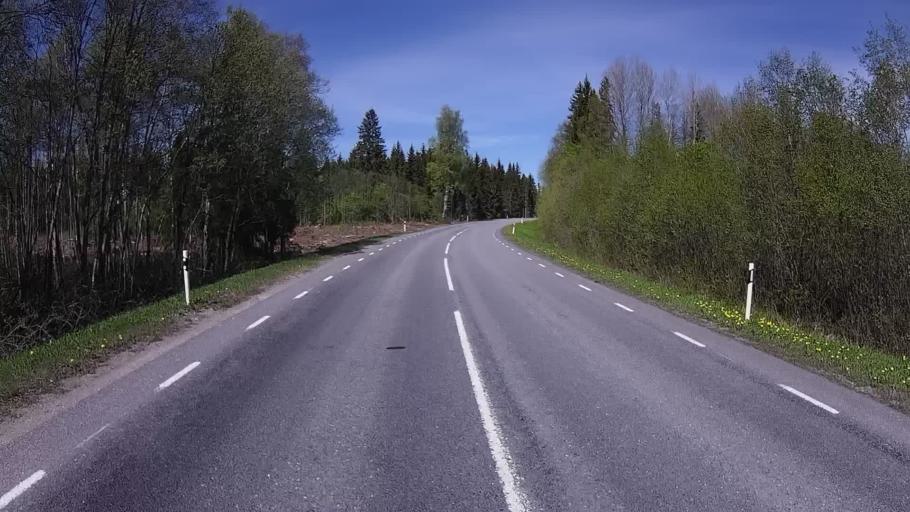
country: EE
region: Raplamaa
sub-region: Kehtna vald
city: Kehtna
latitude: 59.0464
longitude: 25.0242
